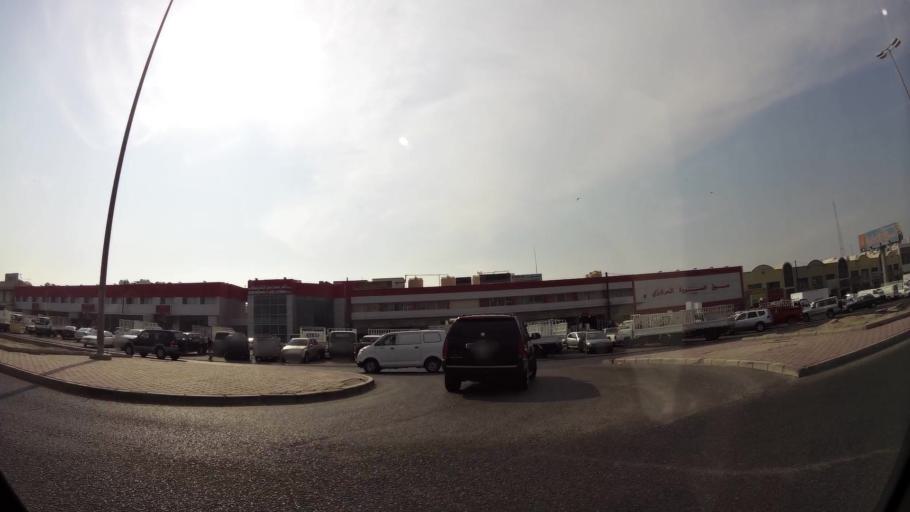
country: KW
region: Al Asimah
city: Ar Rabiyah
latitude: 29.3092
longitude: 47.9483
